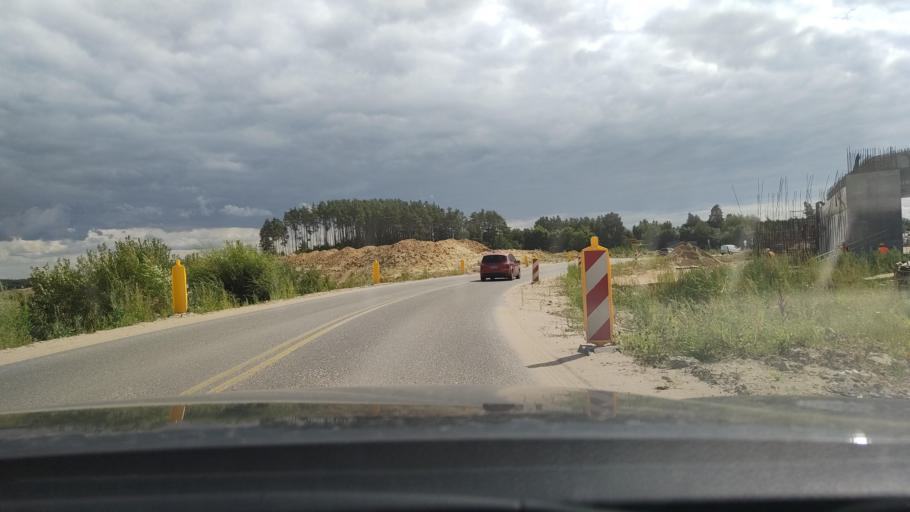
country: PL
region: Pomeranian Voivodeship
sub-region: Powiat wejherowski
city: Bojano
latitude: 54.4659
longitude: 18.3839
